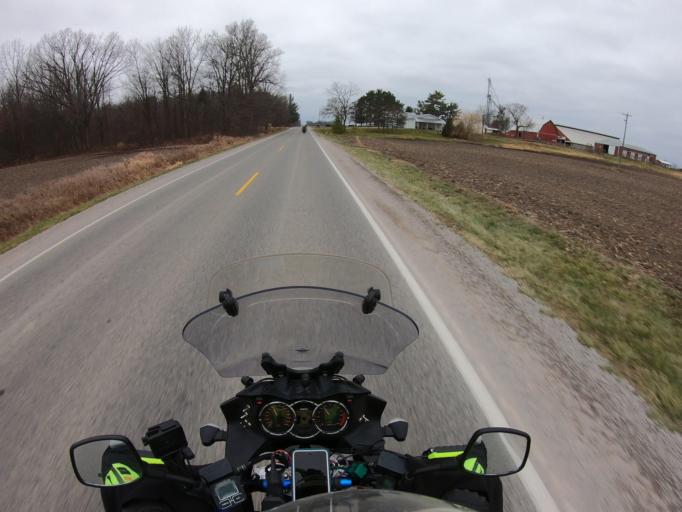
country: US
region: Michigan
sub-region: Saginaw County
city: Saint Charles
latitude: 43.2555
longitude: -84.0944
